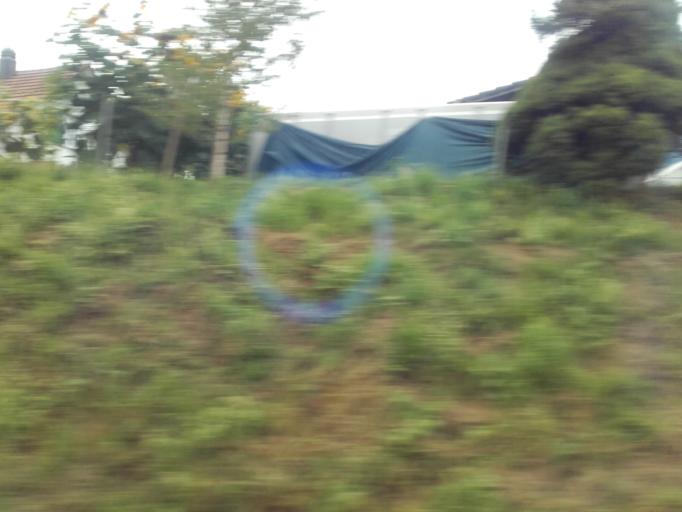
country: CH
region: Solothurn
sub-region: Bezirk Wasseramt
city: Biberist
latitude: 47.1736
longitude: 7.5388
